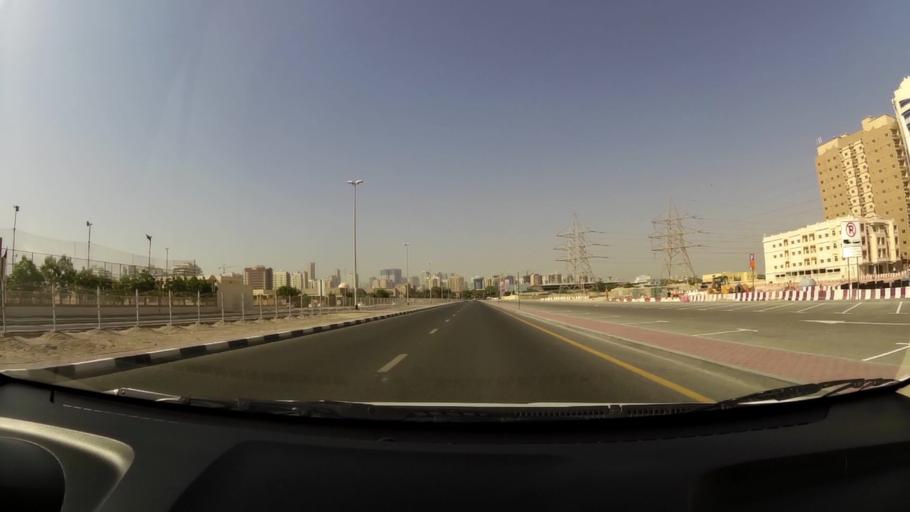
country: AE
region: Ash Shariqah
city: Sharjah
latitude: 25.2811
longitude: 55.3712
